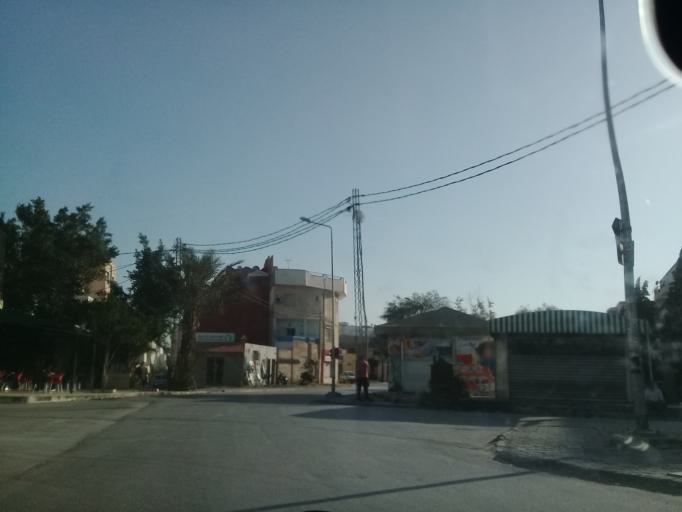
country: TN
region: Ariana
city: Ariana
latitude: 36.8359
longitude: 10.1923
